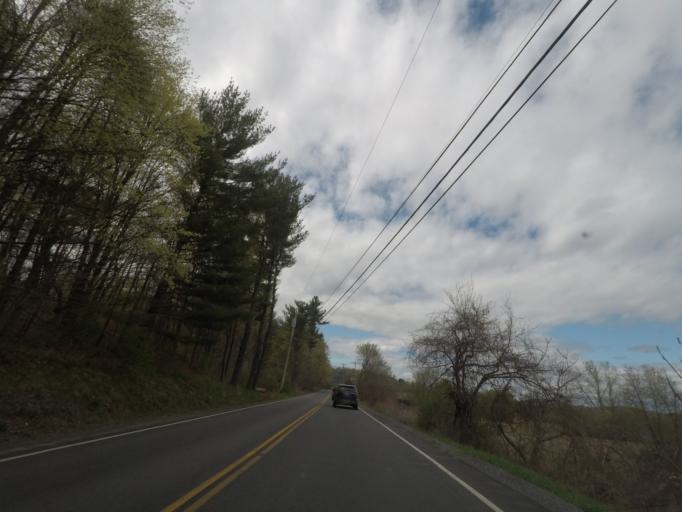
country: US
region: New York
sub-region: Columbia County
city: Valatie
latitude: 42.3831
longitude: -73.6404
